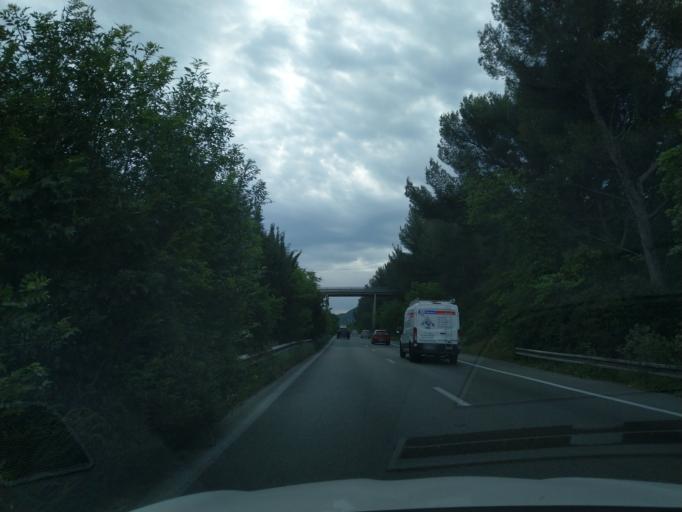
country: FR
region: Provence-Alpes-Cote d'Azur
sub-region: Departement des Bouches-du-Rhone
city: Aubagne
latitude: 43.2875
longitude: 5.5640
